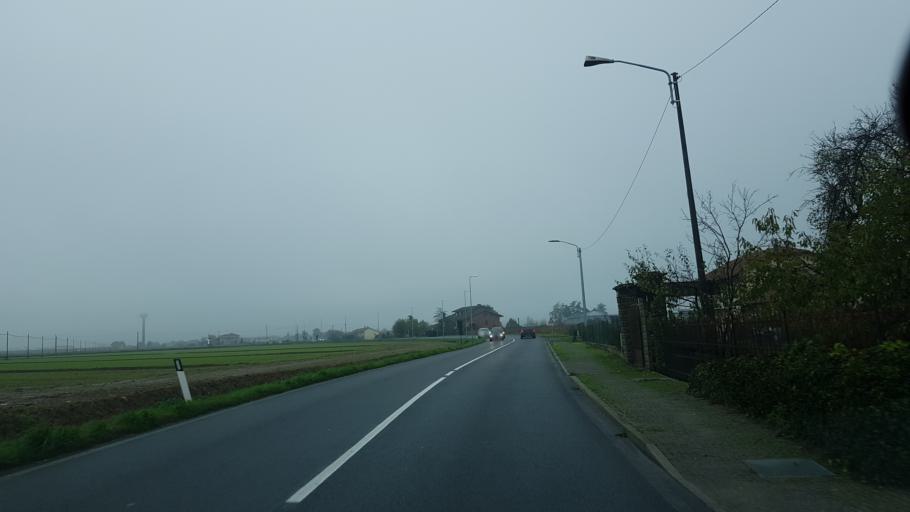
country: IT
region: Piedmont
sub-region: Provincia di Cuneo
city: Vottignasco
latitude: 44.5624
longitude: 7.5768
